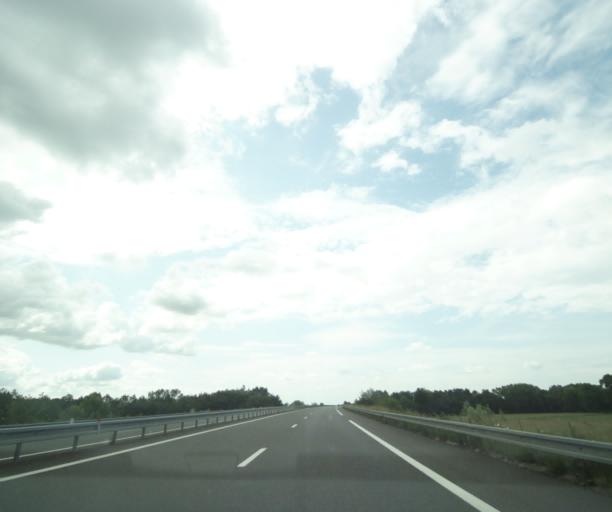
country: FR
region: Pays de la Loire
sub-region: Departement de Maine-et-Loire
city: Vivy
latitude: 47.3402
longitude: -0.0586
